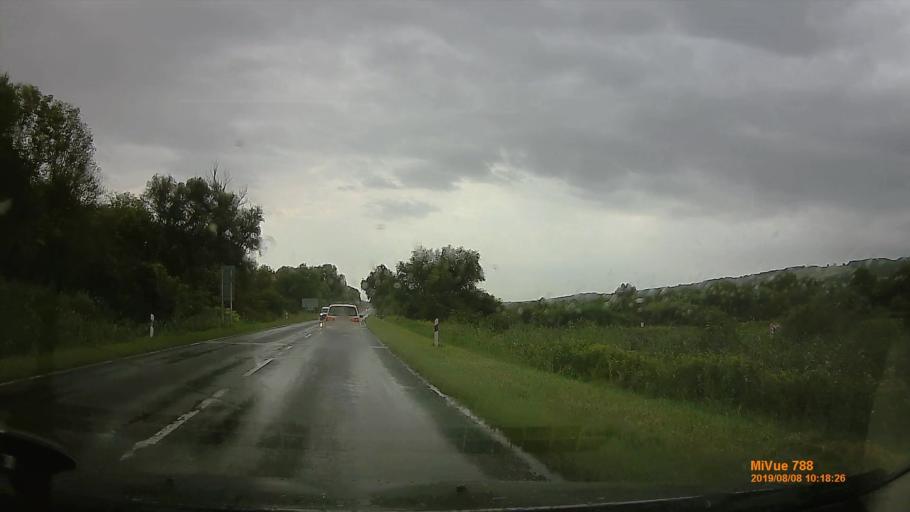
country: HU
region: Zala
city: Zalaegerszeg
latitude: 46.7756
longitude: 16.8584
